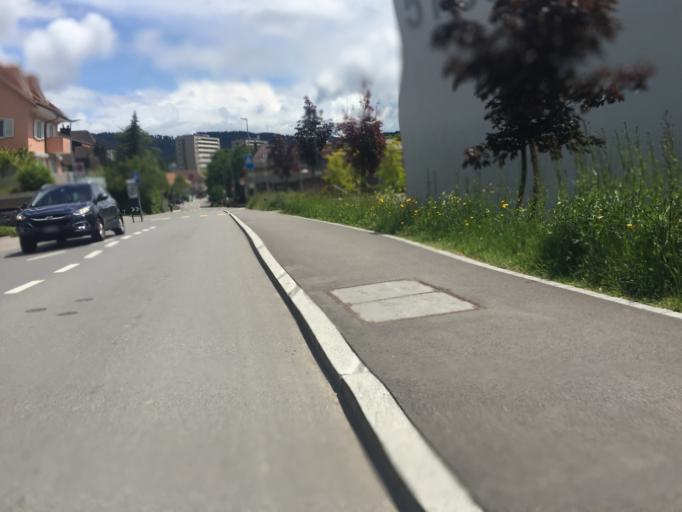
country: CH
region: Bern
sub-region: Bern-Mittelland District
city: Zollikofen
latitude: 46.9981
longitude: 7.4556
